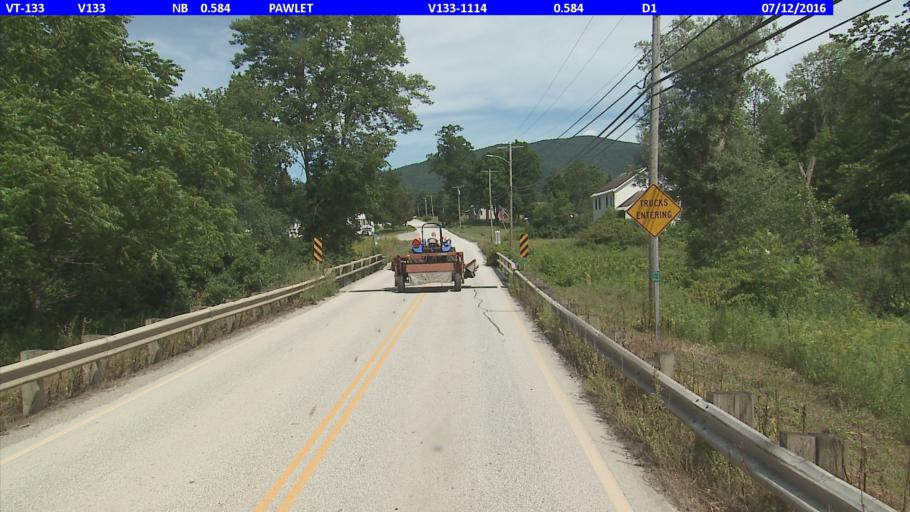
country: US
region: New York
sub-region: Washington County
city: Granville
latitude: 43.3481
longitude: -73.1661
